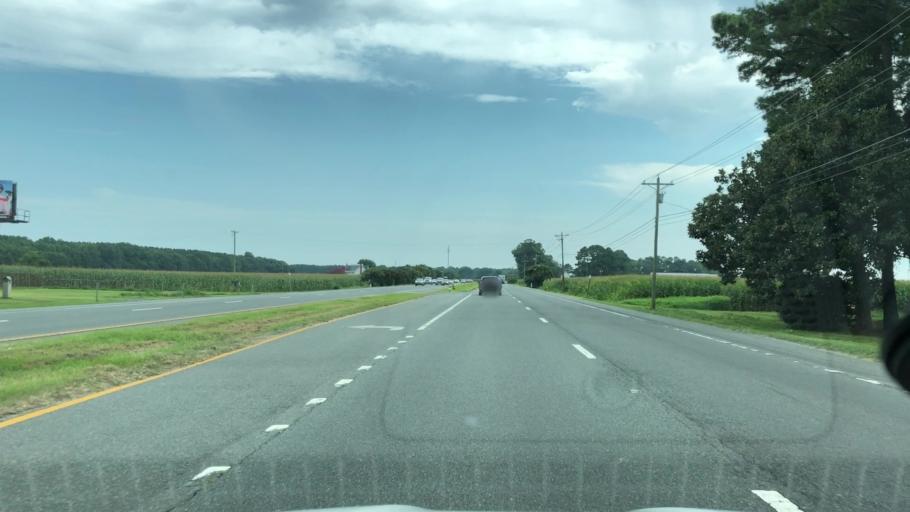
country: US
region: Virginia
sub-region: Accomack County
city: Wattsville
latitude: 37.8677
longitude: -75.5580
